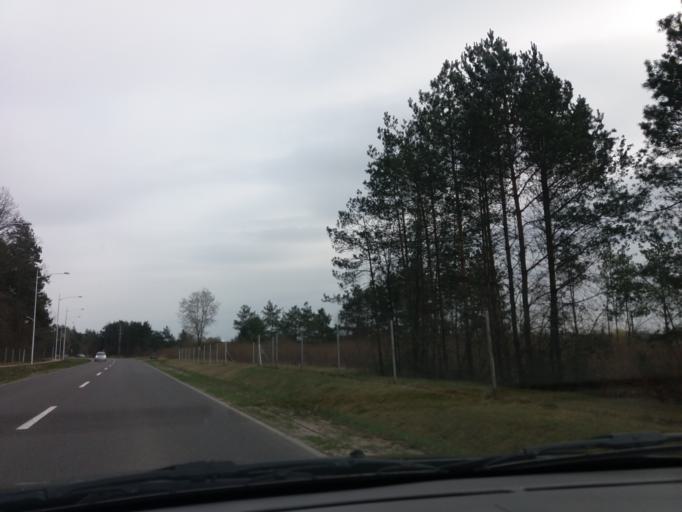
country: PL
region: Masovian Voivodeship
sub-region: Powiat mlawski
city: Mlawa
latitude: 53.1295
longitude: 20.3832
